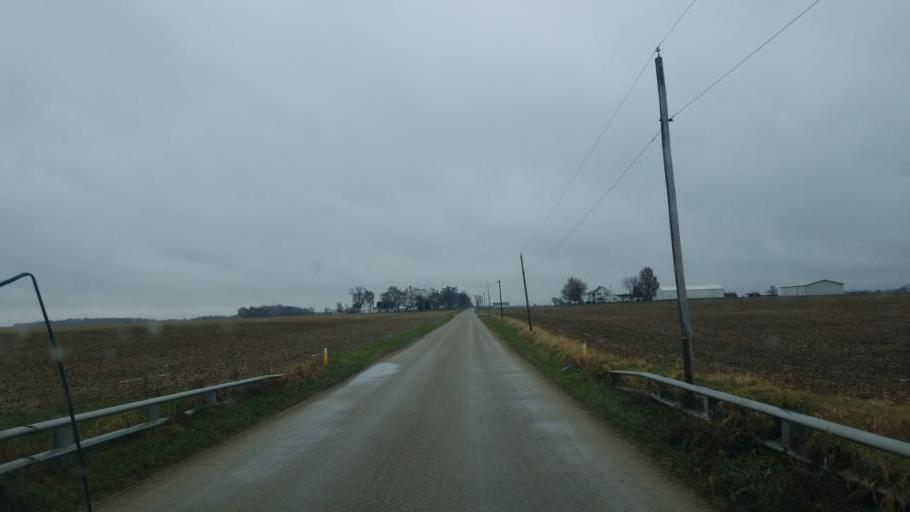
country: US
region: Indiana
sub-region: Adams County
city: Berne
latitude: 40.6749
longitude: -84.9172
